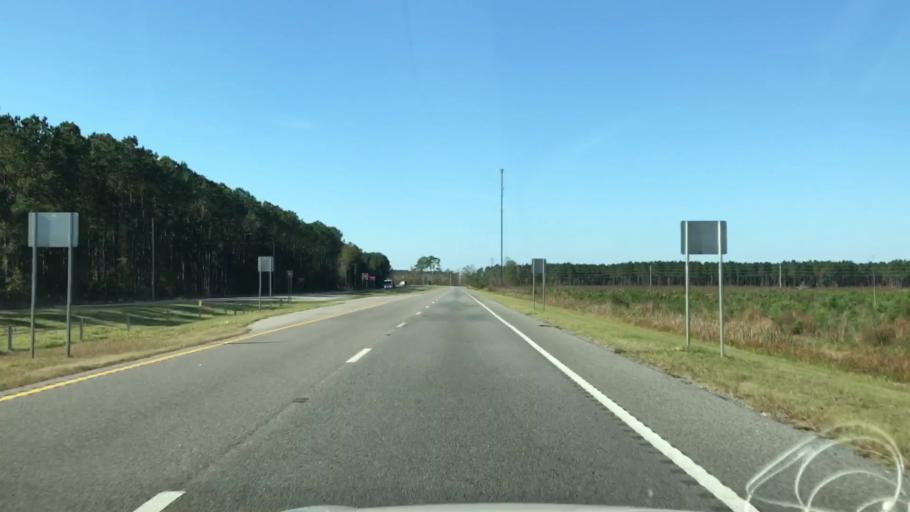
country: US
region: South Carolina
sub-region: Colleton County
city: Walterboro
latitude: 32.7627
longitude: -80.5187
